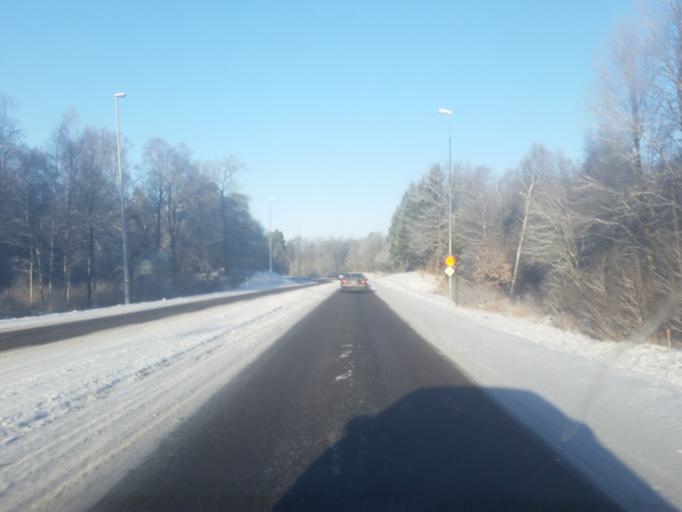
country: SE
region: Vaestra Goetaland
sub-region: Partille Kommun
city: Furulund
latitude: 57.7191
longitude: 12.1397
